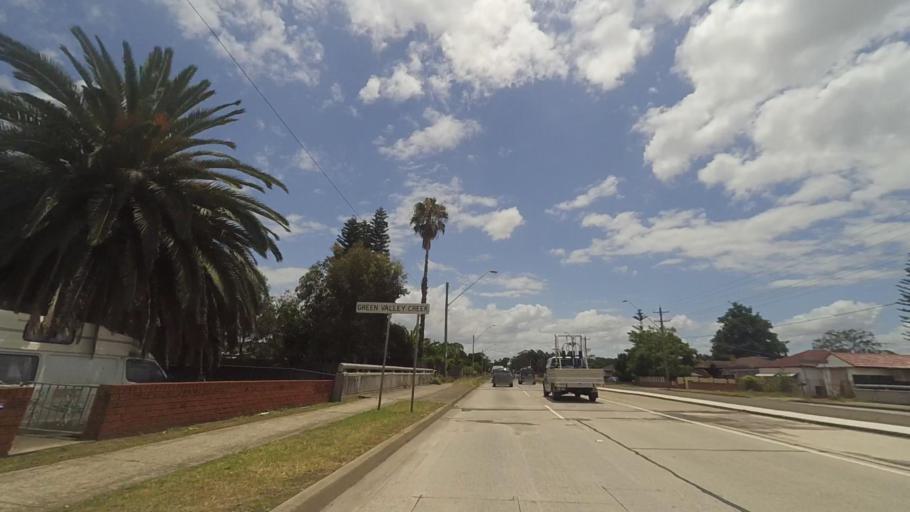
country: AU
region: New South Wales
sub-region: Fairfield
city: Fairfield Heights
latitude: -33.8781
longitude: 150.9249
